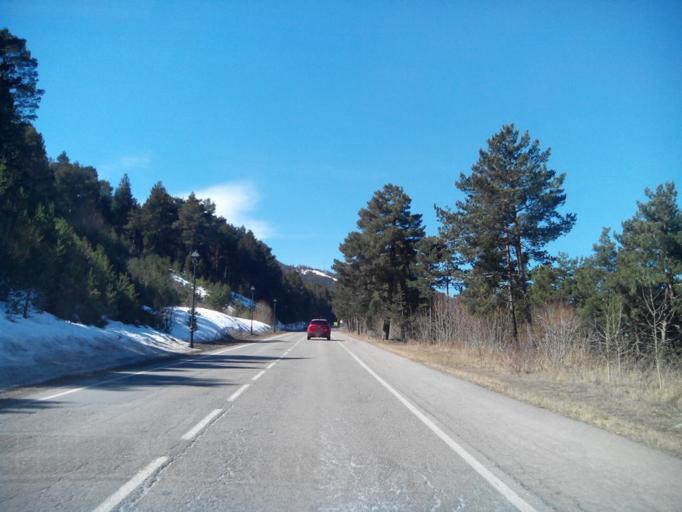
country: ES
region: Catalonia
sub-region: Provincia de Girona
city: Alp
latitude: 42.3440
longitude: 1.9452
